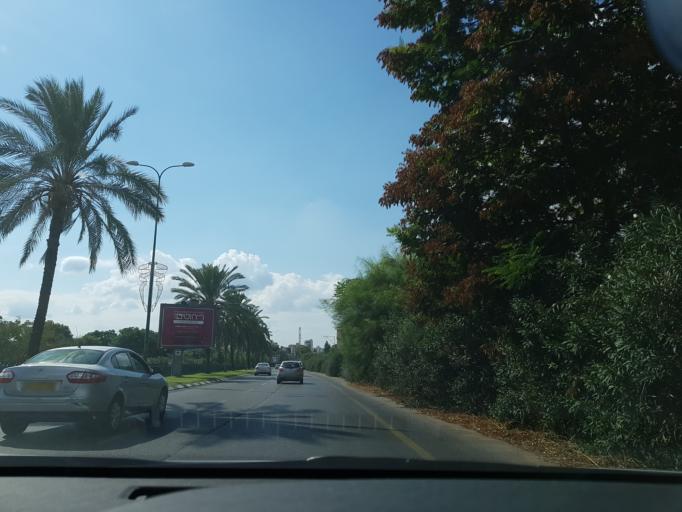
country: IL
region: Central District
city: Ness Ziona
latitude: 31.9358
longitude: 34.7997
